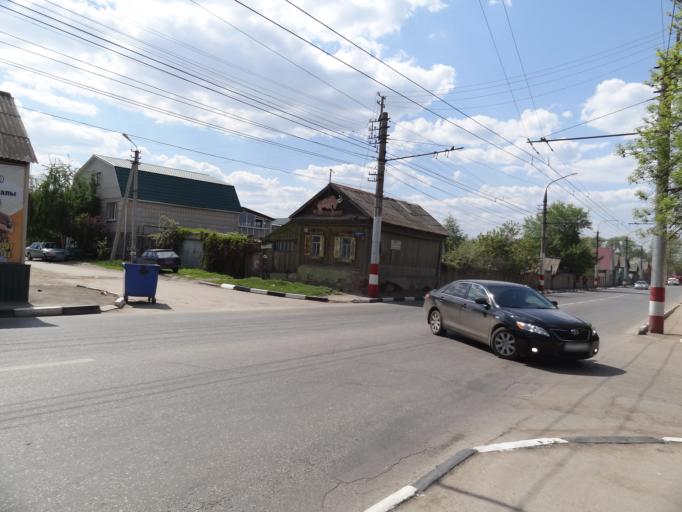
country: RU
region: Saratov
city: Engel's
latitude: 51.5014
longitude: 46.1084
